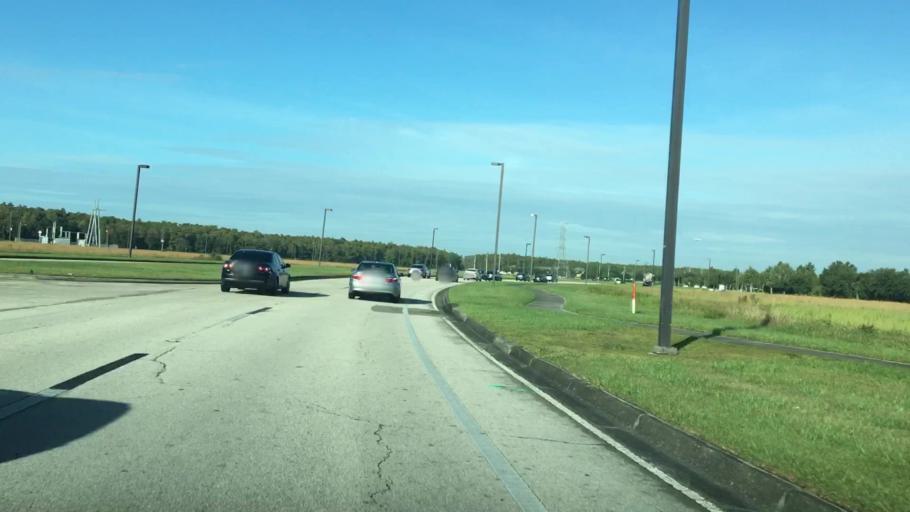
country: US
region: Florida
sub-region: Orange County
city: Conway
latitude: 28.4645
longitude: -81.2833
